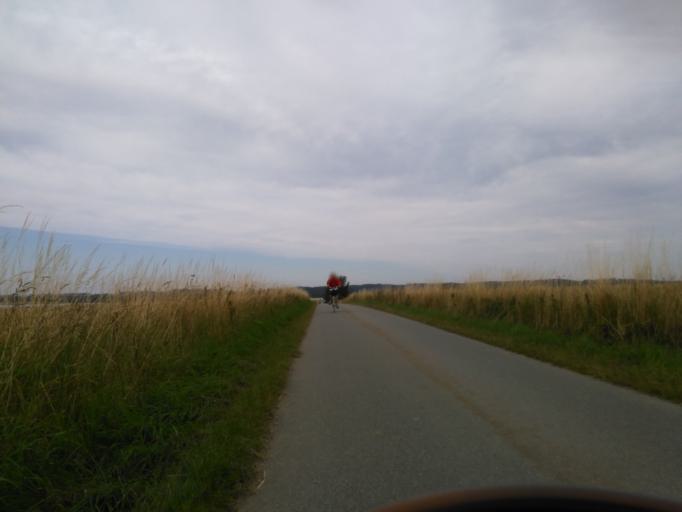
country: DK
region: Central Jutland
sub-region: Odder Kommune
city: Odder
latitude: 55.8596
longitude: 10.0624
